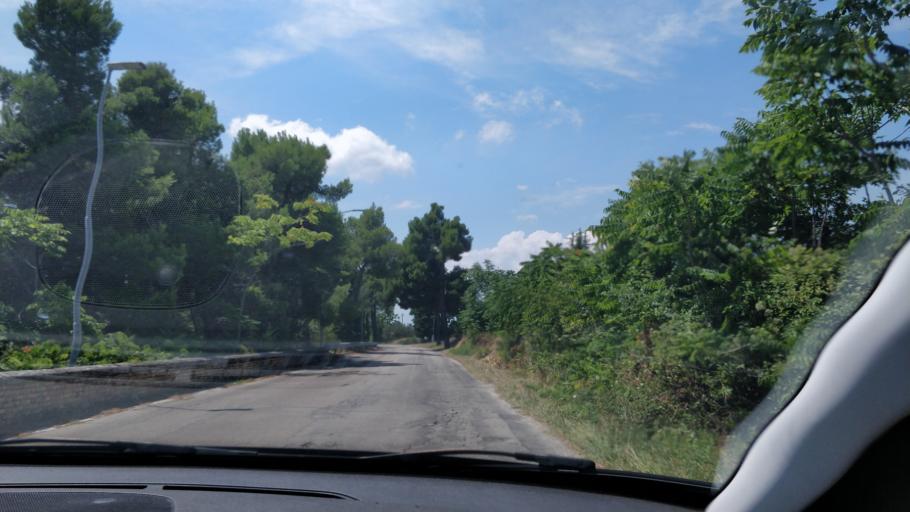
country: IT
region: Abruzzo
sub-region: Provincia di Chieti
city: Torrevecchia
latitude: 42.4078
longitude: 14.2233
